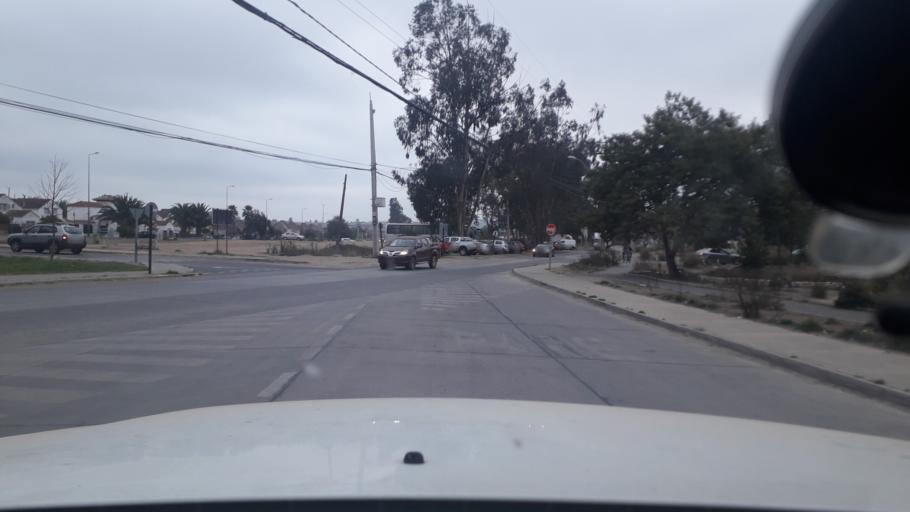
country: CL
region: Valparaiso
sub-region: Provincia de Valparaiso
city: Vina del Mar
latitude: -33.1257
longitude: -71.5709
